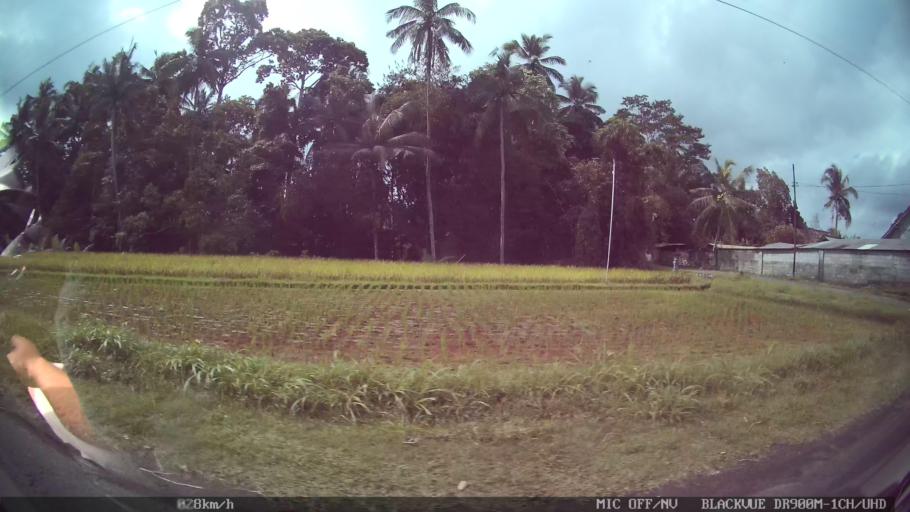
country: ID
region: Bali
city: Banjar Pesalakan
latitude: -8.4820
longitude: 115.3009
